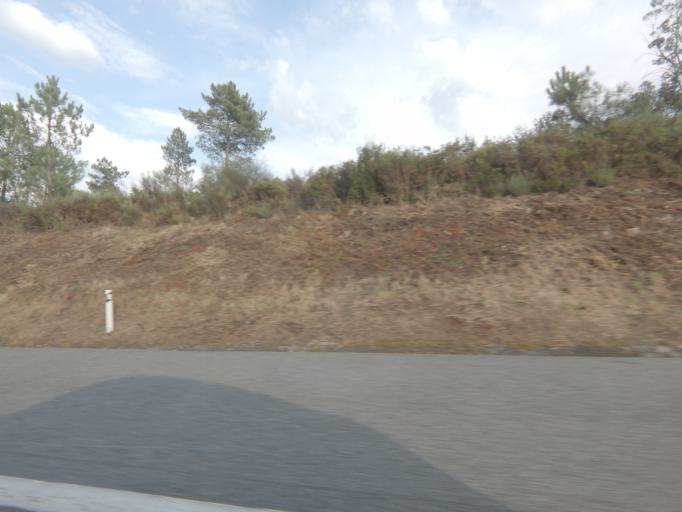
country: PT
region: Viseu
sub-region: Castro Daire
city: Castro Daire
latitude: 40.8404
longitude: -7.9283
